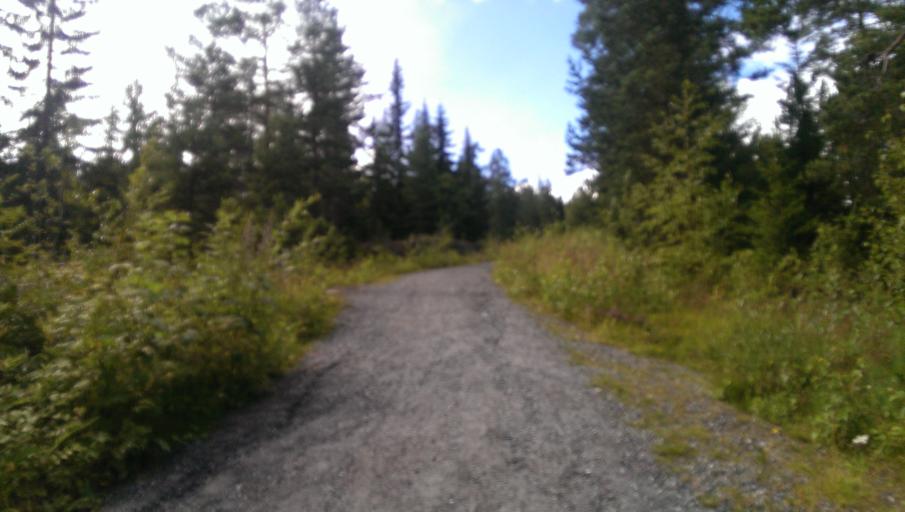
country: NO
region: Buskerud
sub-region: Kongsberg
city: Kongsberg
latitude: 59.6531
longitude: 9.6087
